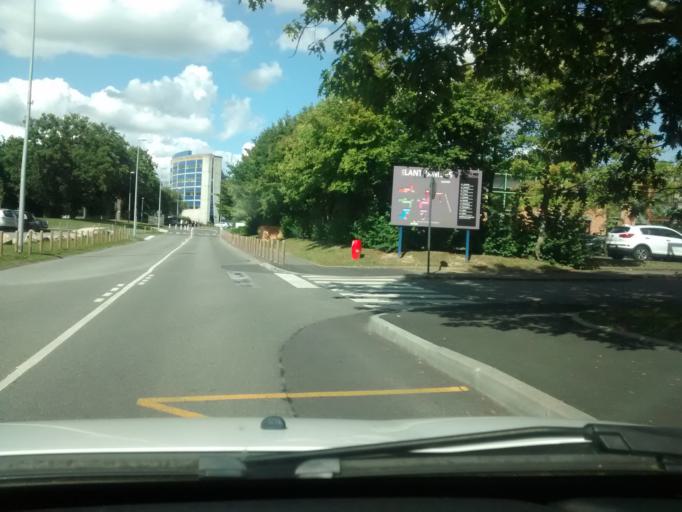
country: FR
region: Brittany
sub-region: Departement d'Ille-et-Vilaine
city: Cesson-Sevigne
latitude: 48.1319
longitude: -1.6244
